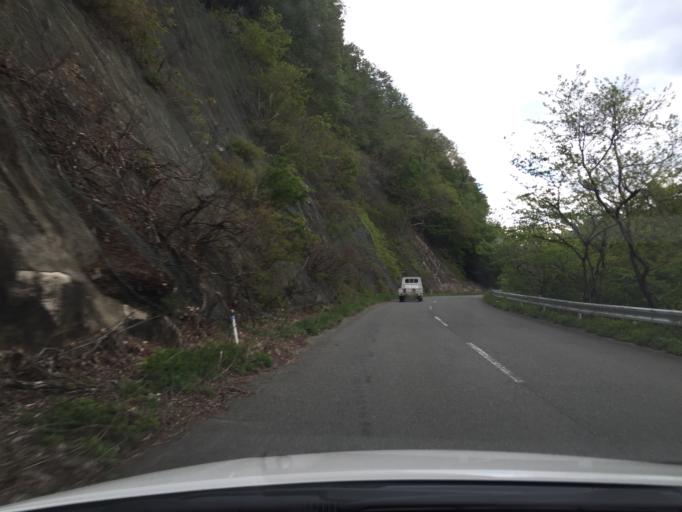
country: JP
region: Miyagi
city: Marumori
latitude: 37.7231
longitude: 140.7979
